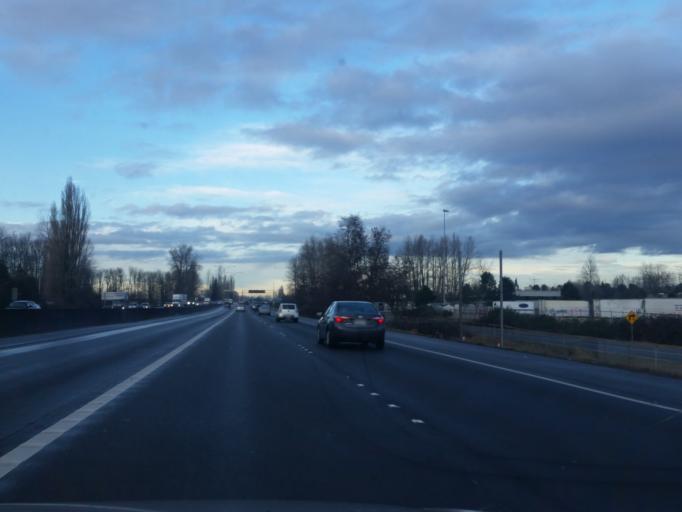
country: US
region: Washington
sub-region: King County
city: Kent
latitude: 47.3651
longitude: -122.2445
